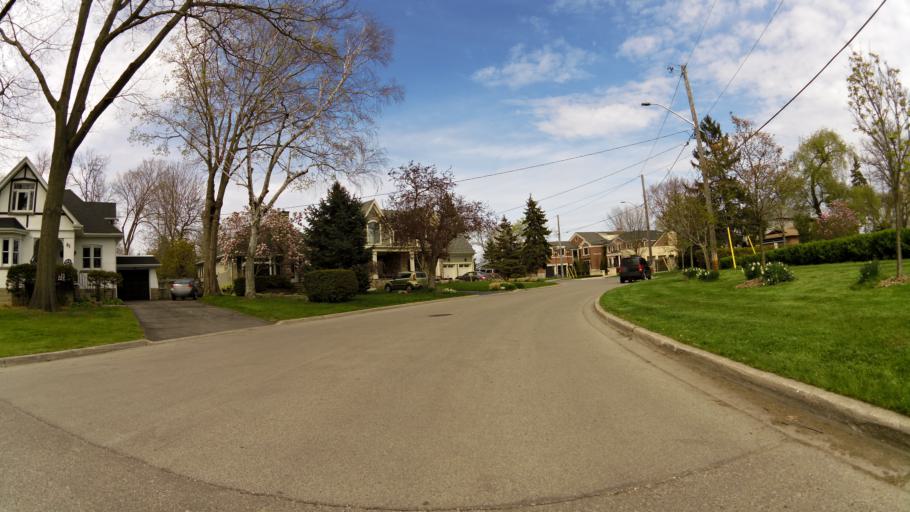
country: CA
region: Ontario
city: Mississauga
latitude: 43.5585
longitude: -79.5720
